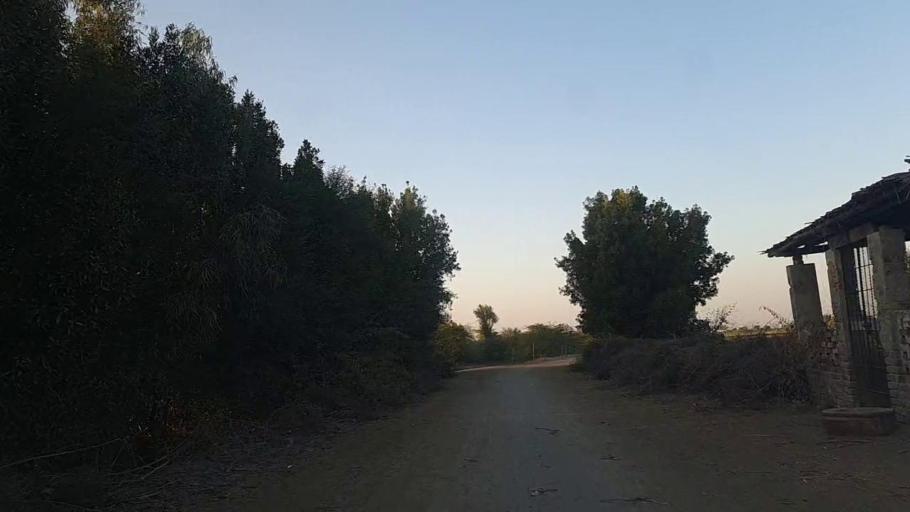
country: PK
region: Sindh
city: Naukot
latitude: 25.0387
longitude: 69.4099
